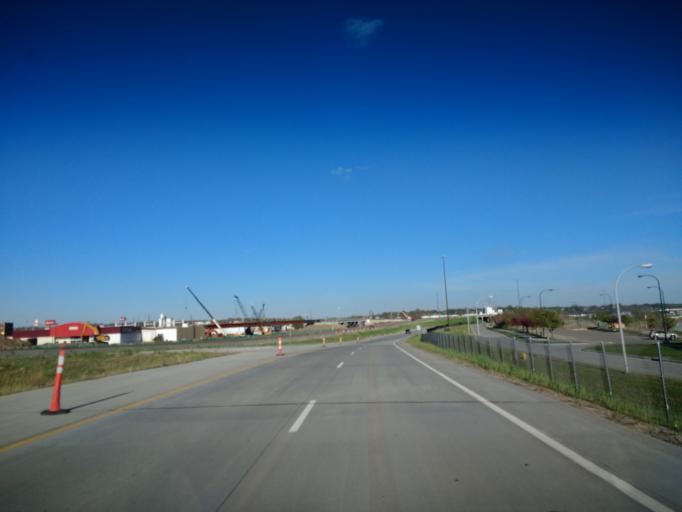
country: US
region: Iowa
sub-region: Woodbury County
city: Sioux City
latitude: 42.4883
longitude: -96.4026
